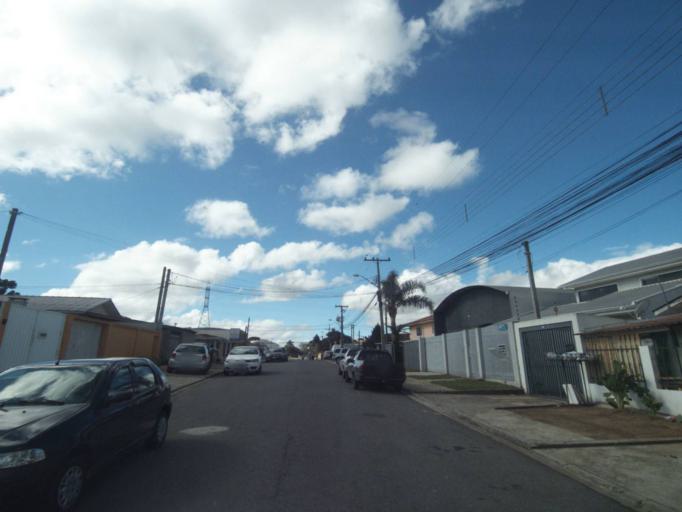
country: BR
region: Parana
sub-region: Sao Jose Dos Pinhais
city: Sao Jose dos Pinhais
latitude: -25.5312
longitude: -49.2894
